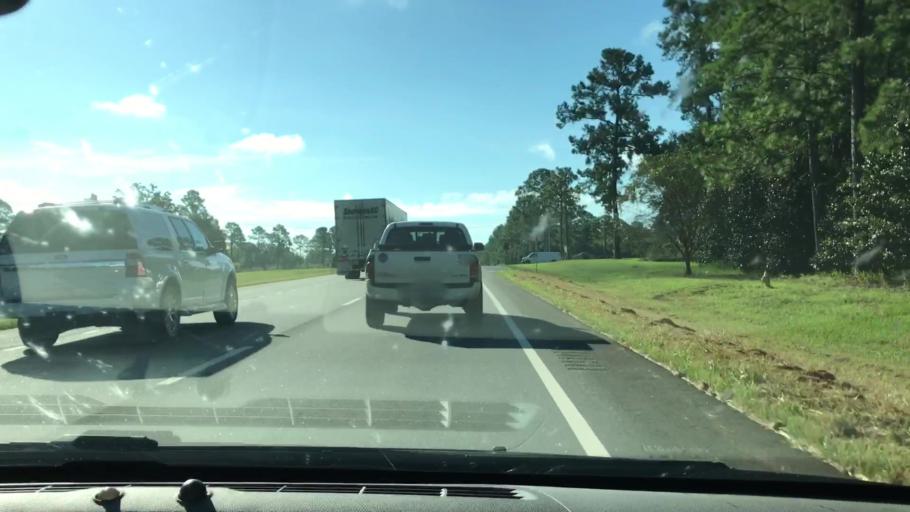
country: US
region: Georgia
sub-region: Lee County
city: Leesburg
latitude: 31.6480
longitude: -84.2611
